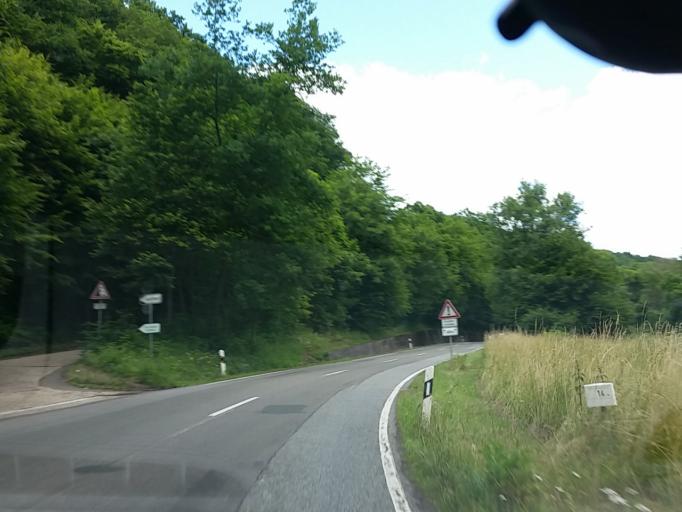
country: DE
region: Saarland
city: Schmelz
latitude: 49.4731
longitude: 6.8596
